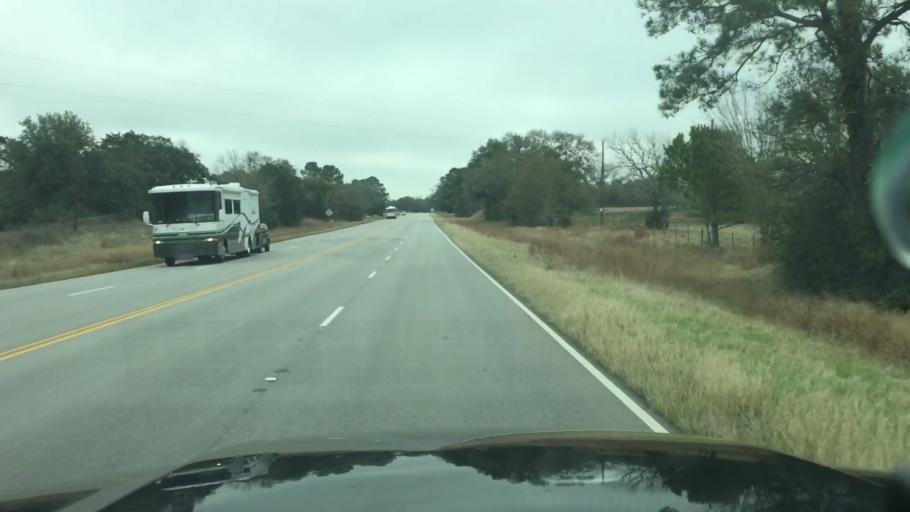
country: US
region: Texas
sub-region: Lee County
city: Giddings
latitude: 30.0881
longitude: -96.9148
